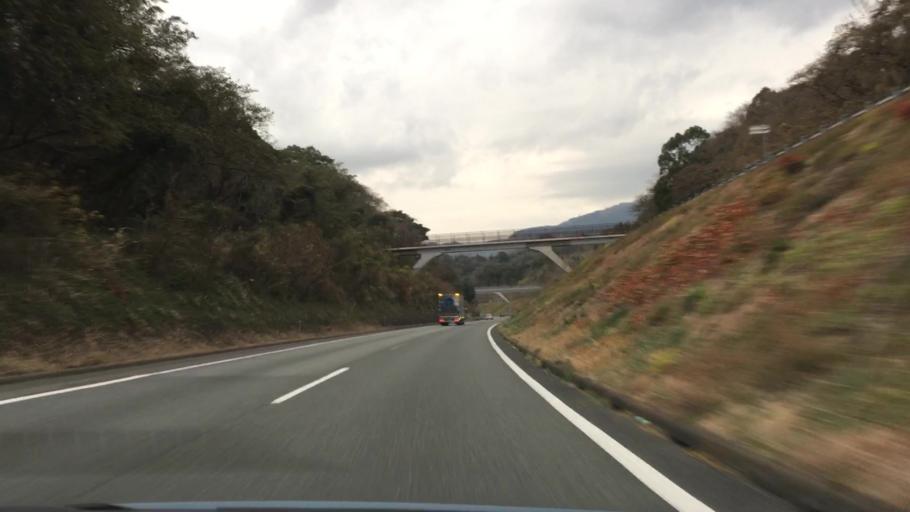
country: JP
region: Shizuoka
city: Fuji
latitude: 35.1204
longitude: 138.6006
